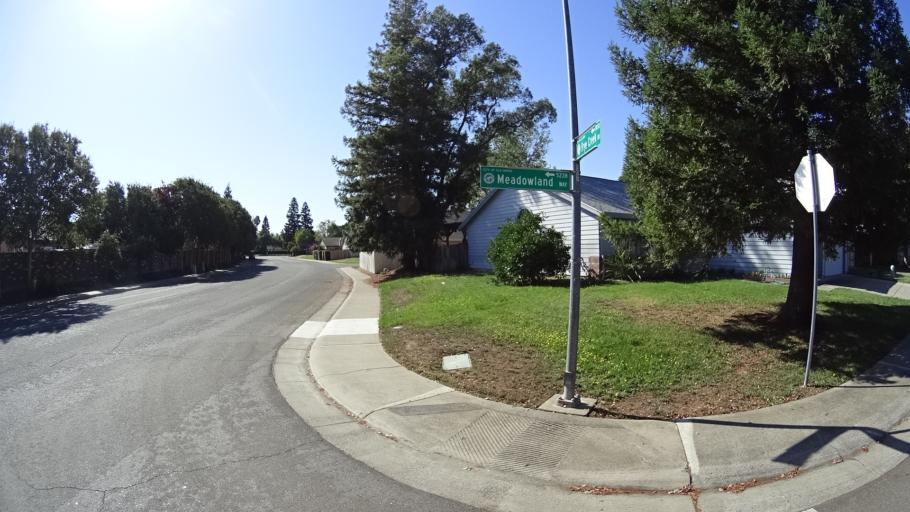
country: US
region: California
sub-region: Sacramento County
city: Laguna
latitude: 38.4364
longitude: -121.4427
